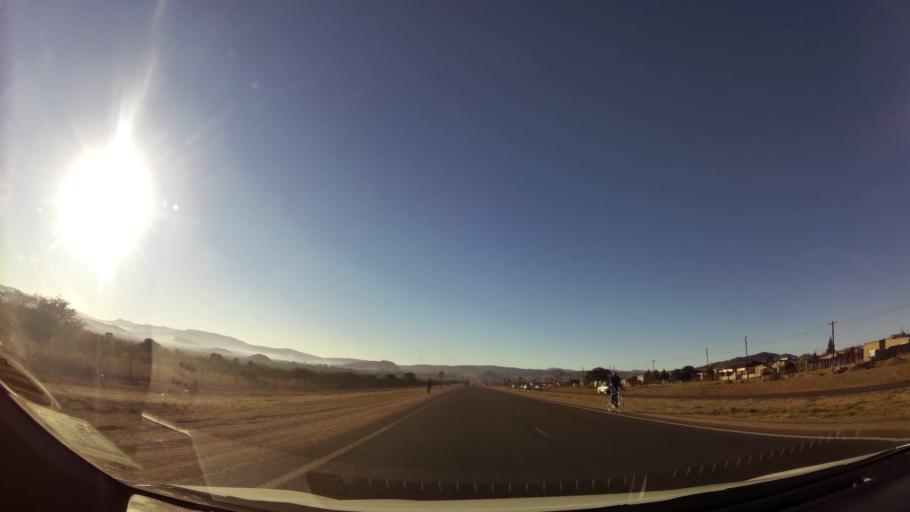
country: ZA
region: Limpopo
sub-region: Capricorn District Municipality
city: Mankoeng
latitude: -23.9005
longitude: 29.7410
